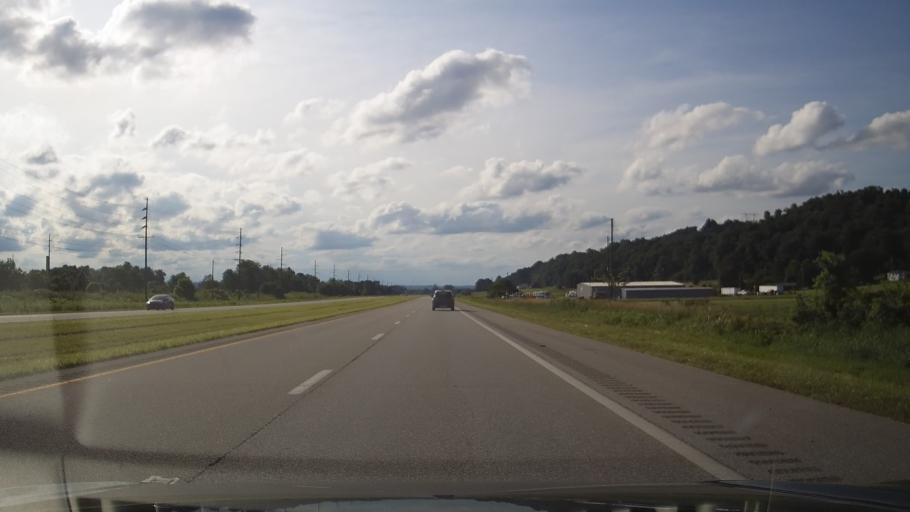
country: US
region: Kentucky
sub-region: Greenup County
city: Greenup
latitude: 38.5945
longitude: -82.8100
